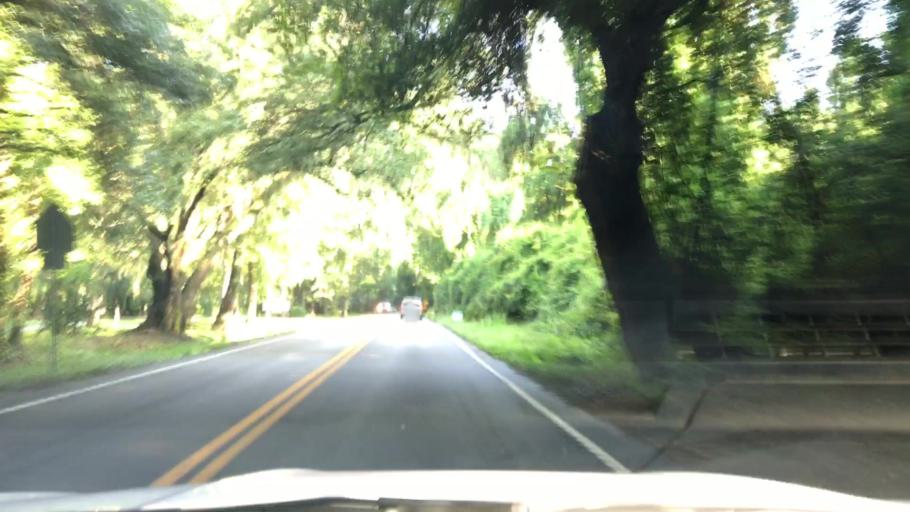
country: US
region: South Carolina
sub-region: Charleston County
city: Shell Point
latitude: 32.8576
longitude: -80.0745
